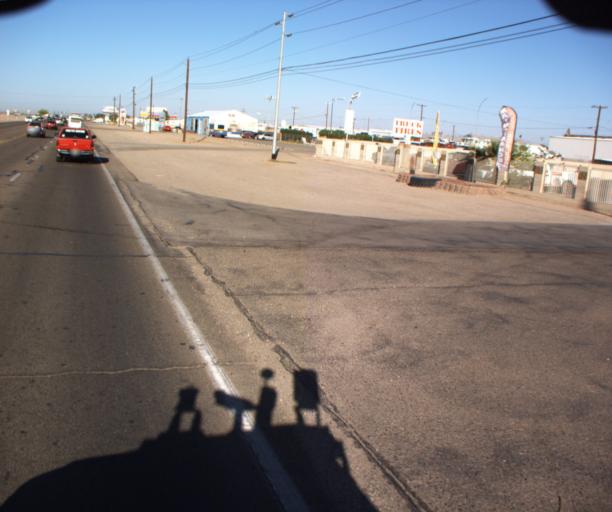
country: US
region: Arizona
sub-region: Yuma County
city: Yuma
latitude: 32.6698
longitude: -114.5743
